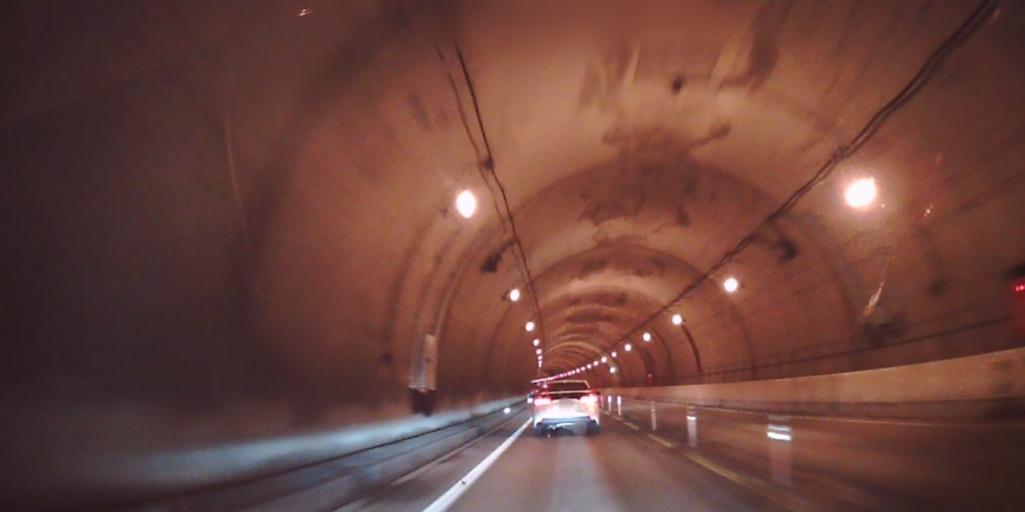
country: JP
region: Hokkaido
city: Date
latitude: 42.5538
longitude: 140.7857
